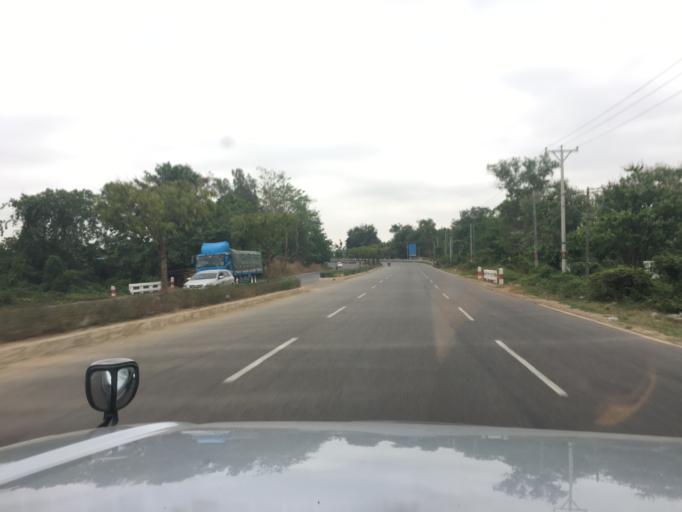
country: MM
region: Bago
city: Thanatpin
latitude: 17.2173
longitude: 96.4280
